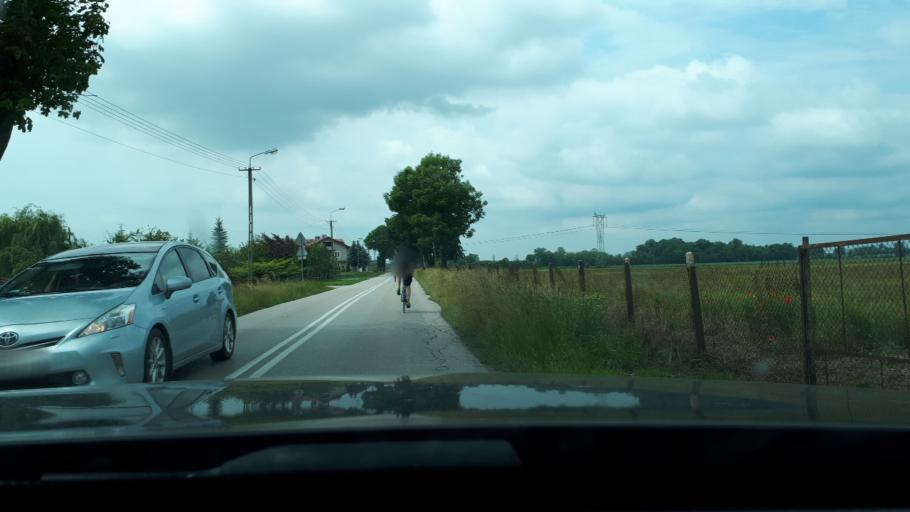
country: PL
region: Masovian Voivodeship
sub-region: Powiat warszawski zachodni
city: Blonie
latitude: 52.2369
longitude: 20.6566
